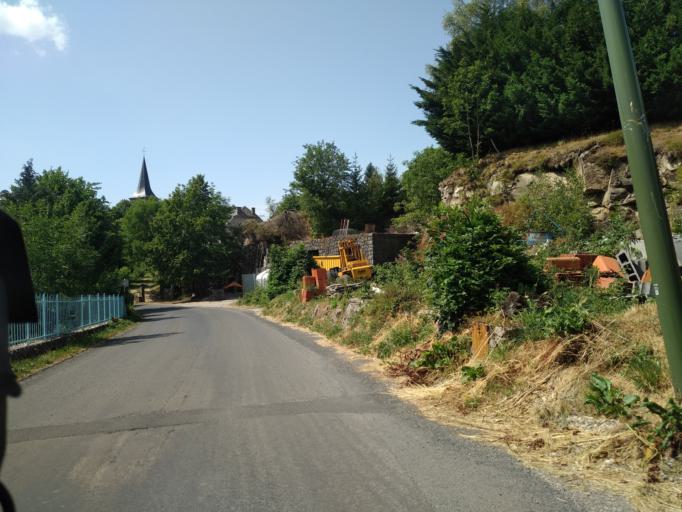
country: FR
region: Auvergne
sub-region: Departement du Cantal
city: Riom-es-Montagnes
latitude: 45.1624
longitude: 2.7072
